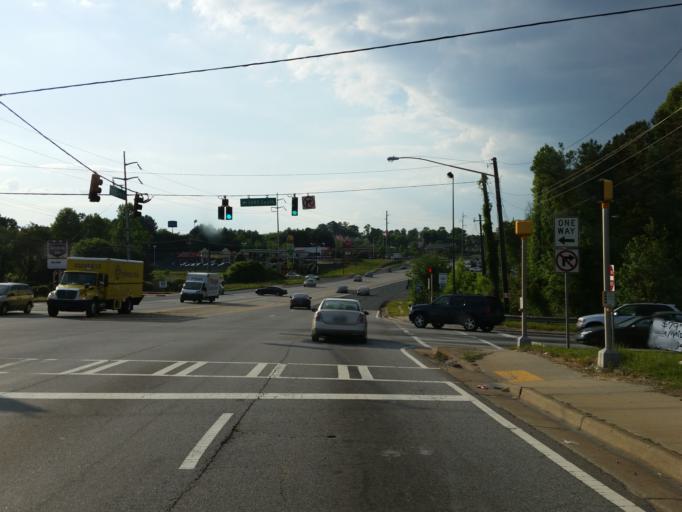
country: US
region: Georgia
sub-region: Cobb County
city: Vinings
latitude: 33.8256
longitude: -84.4898
